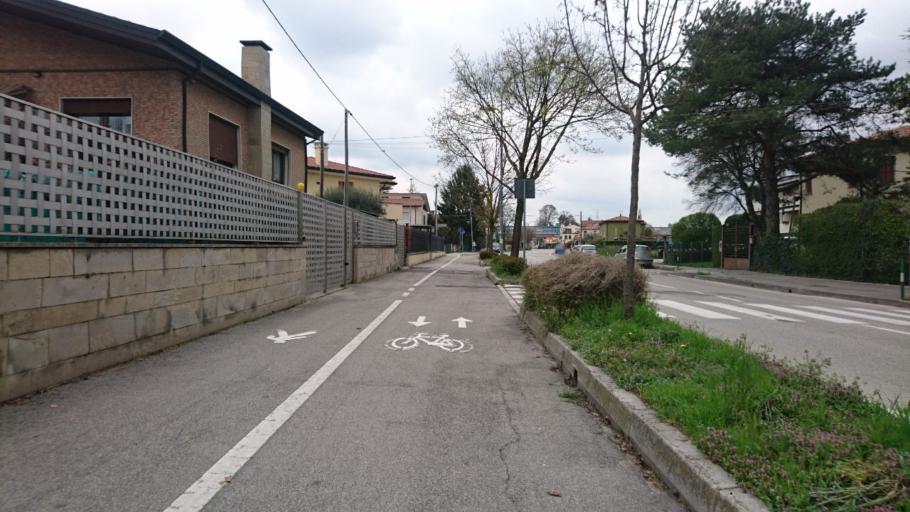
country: IT
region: Veneto
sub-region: Provincia di Padova
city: Vigodarzere
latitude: 45.4407
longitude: 11.8704
